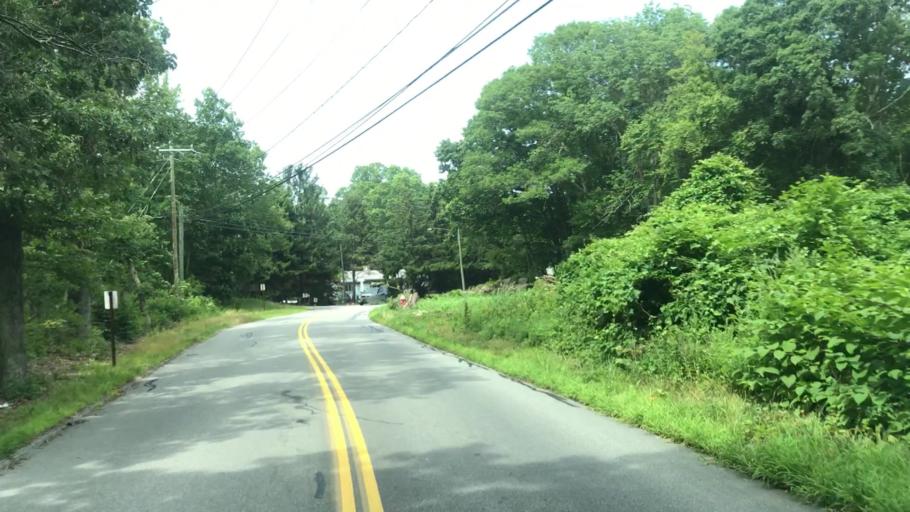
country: US
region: Connecticut
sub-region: New London County
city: Niantic
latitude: 41.3348
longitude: -72.2188
